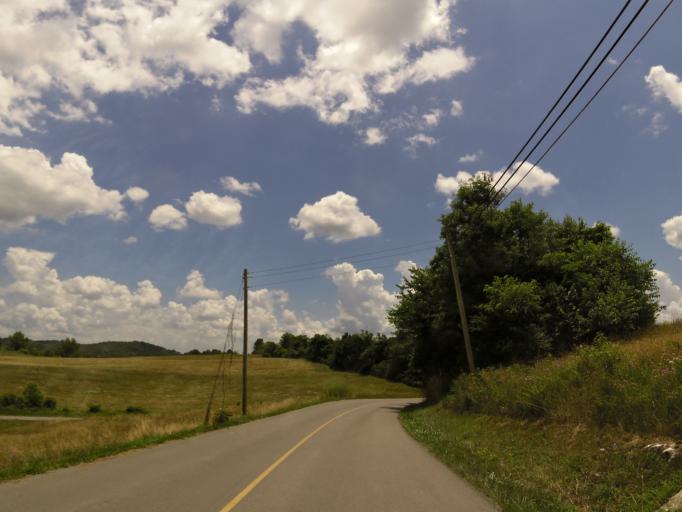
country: US
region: Tennessee
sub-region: Claiborne County
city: New Tazewell
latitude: 36.4384
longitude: -83.5985
